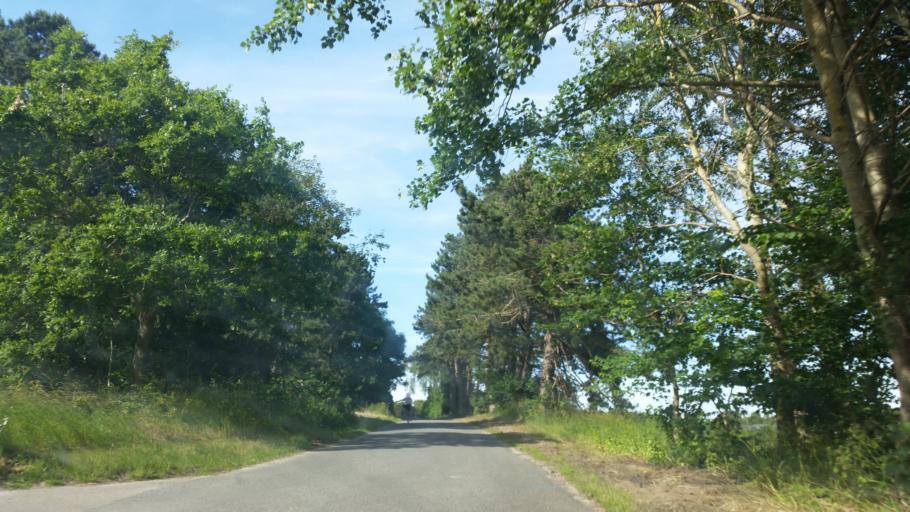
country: DK
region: Central Jutland
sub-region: Samso Kommune
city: Tranebjerg
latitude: 55.8211
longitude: 10.5383
